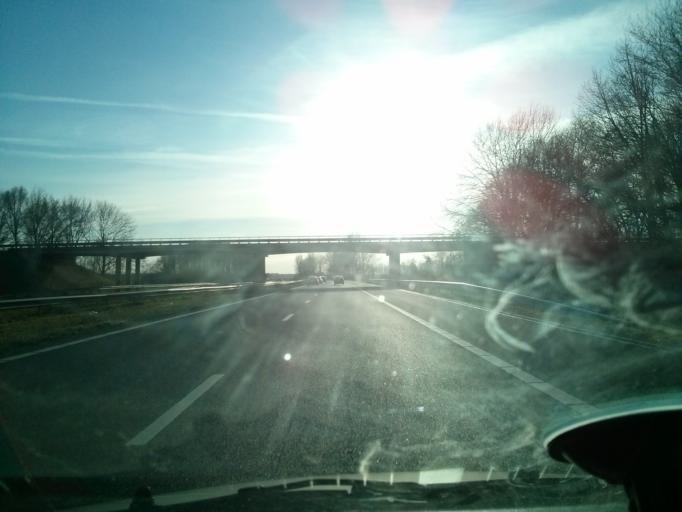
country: NL
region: North Brabant
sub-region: Gemeente Landerd
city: Schaijk
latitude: 51.7844
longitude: 5.6450
